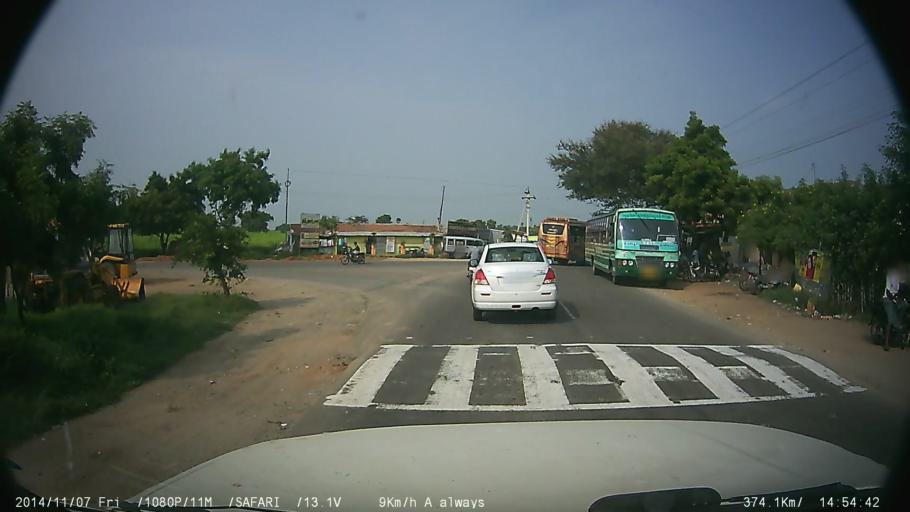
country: IN
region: Tamil Nadu
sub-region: Tiruppur
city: Uttukkuli
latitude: 11.1581
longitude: 77.4273
